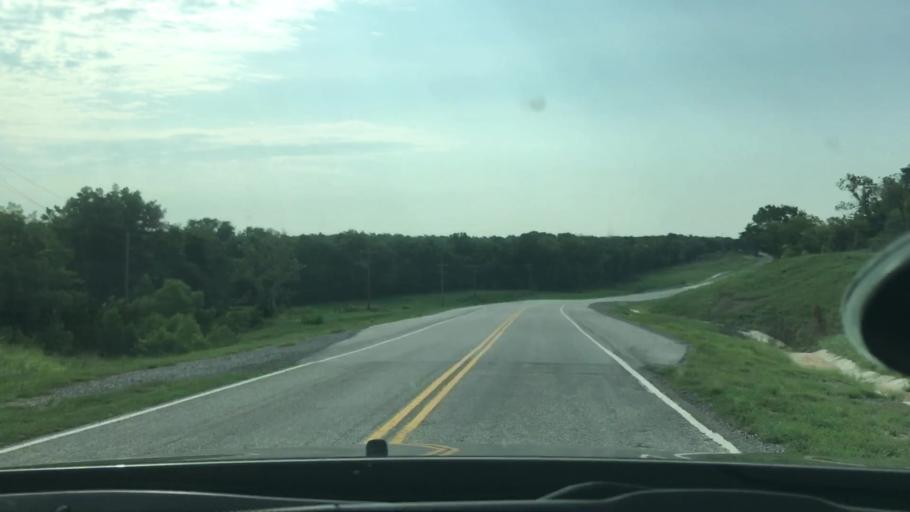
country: US
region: Oklahoma
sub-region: Johnston County
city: Tishomingo
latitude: 34.1632
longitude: -96.5686
